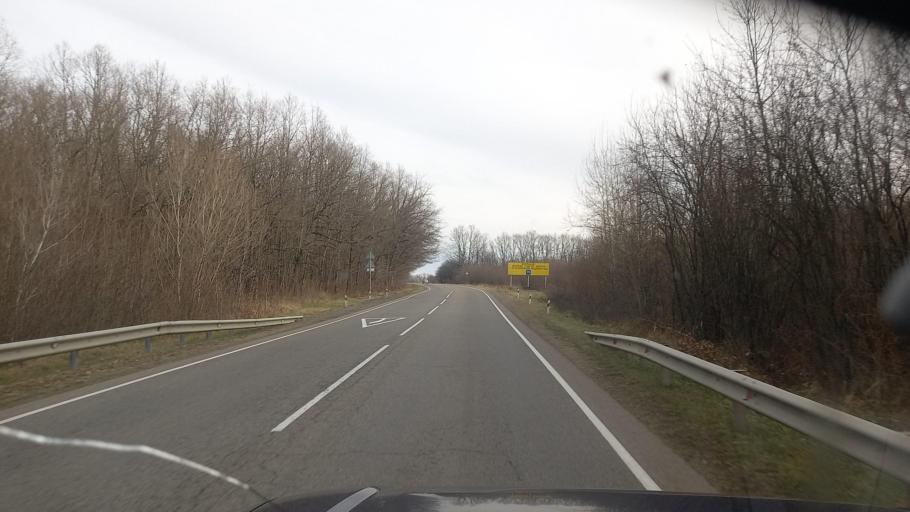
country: RU
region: Adygeya
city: Ponezhukay
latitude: 44.6741
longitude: 39.4466
